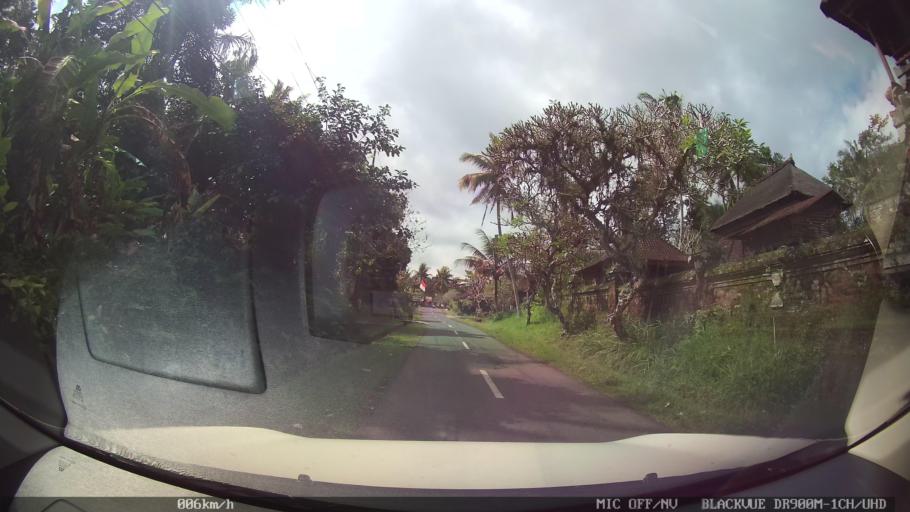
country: ID
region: Bali
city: Banjar Pesalakan
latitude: -8.5130
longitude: 115.3021
